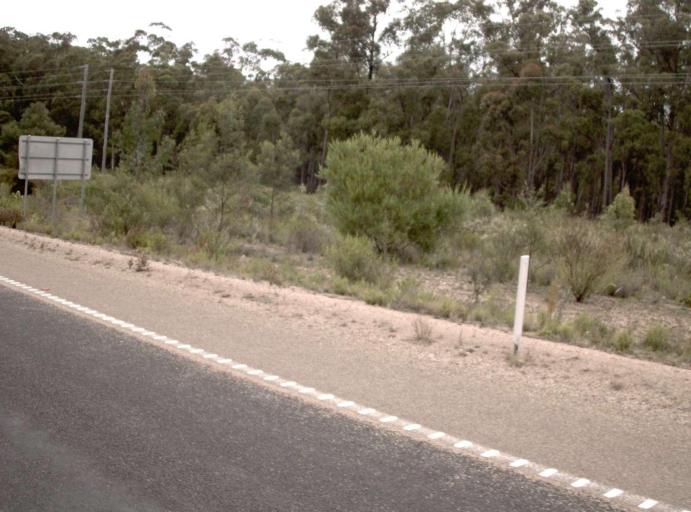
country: AU
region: Victoria
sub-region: East Gippsland
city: Lakes Entrance
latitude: -37.7008
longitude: 148.0503
